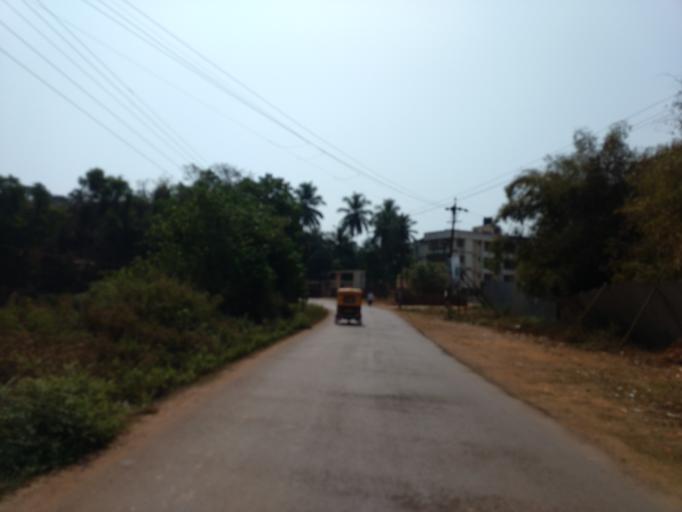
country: IN
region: Maharashtra
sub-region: Sindhudurg
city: Kudal
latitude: 16.0152
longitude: 73.6831
